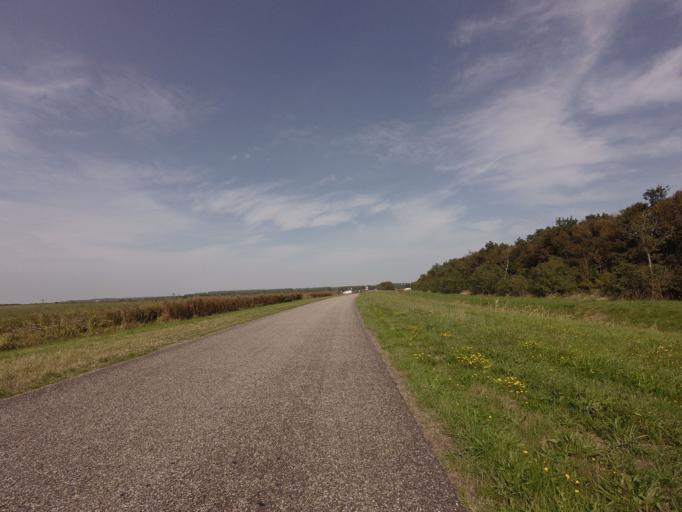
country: NL
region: Groningen
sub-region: Gemeente De Marne
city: Ulrum
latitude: 53.3592
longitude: 6.2611
